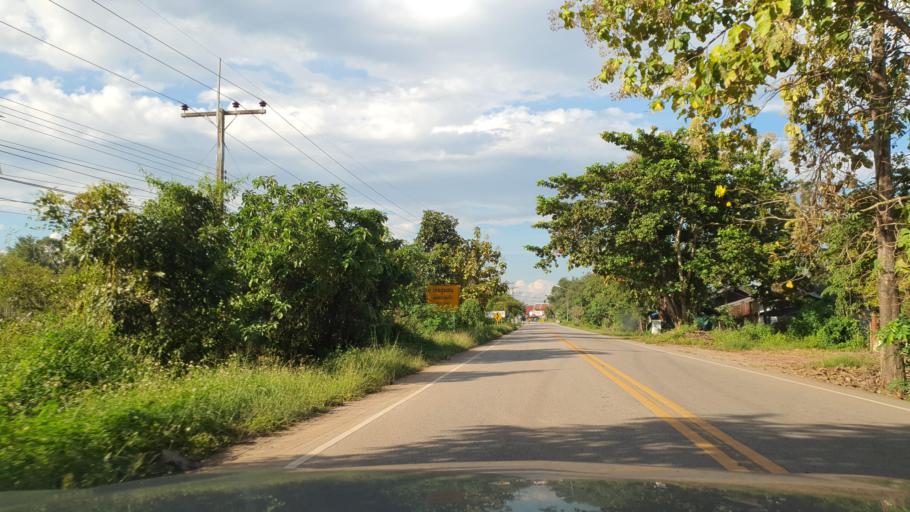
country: TH
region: Phayao
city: Phayao
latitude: 19.1449
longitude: 99.8338
